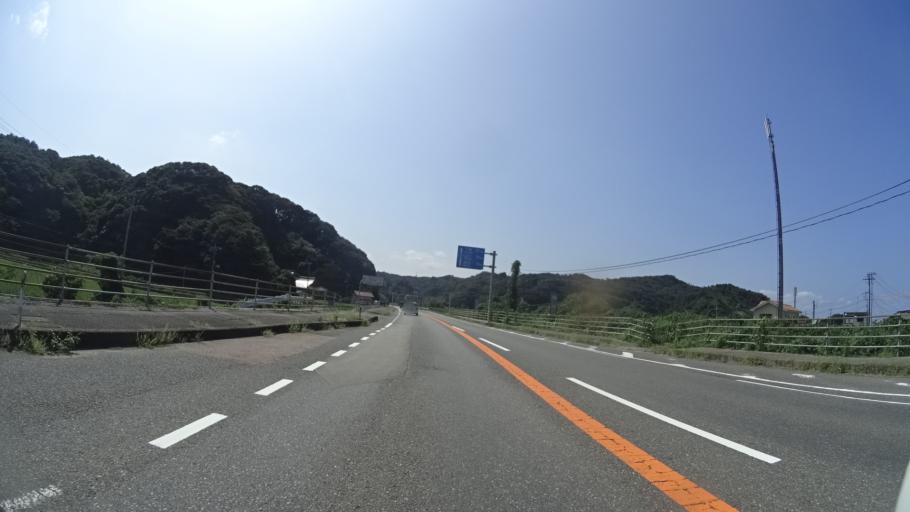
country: JP
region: Shimane
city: Masuda
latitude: 34.7322
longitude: 131.8731
